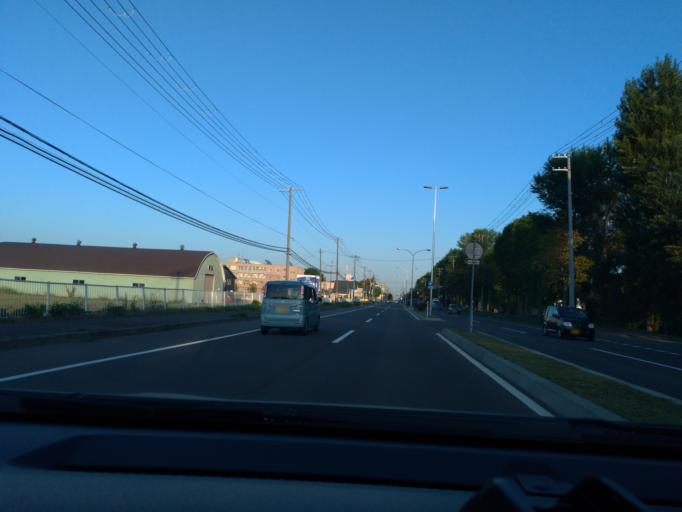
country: JP
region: Hokkaido
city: Ishikari
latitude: 43.1598
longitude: 141.3791
